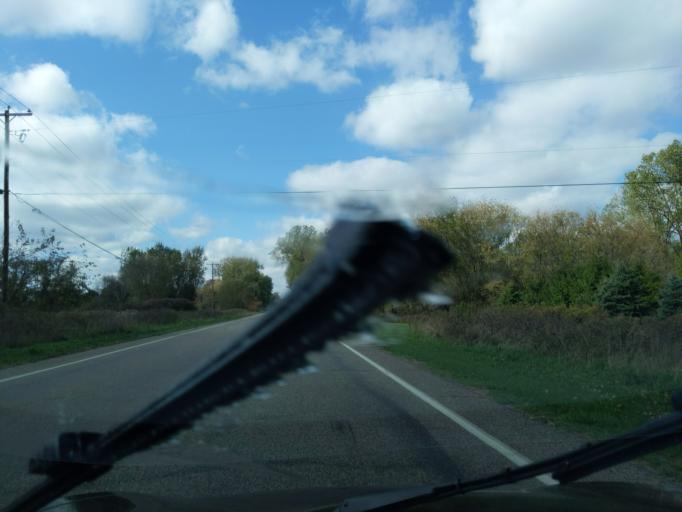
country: US
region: Michigan
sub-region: Eaton County
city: Charlotte
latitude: 42.5675
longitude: -84.7955
